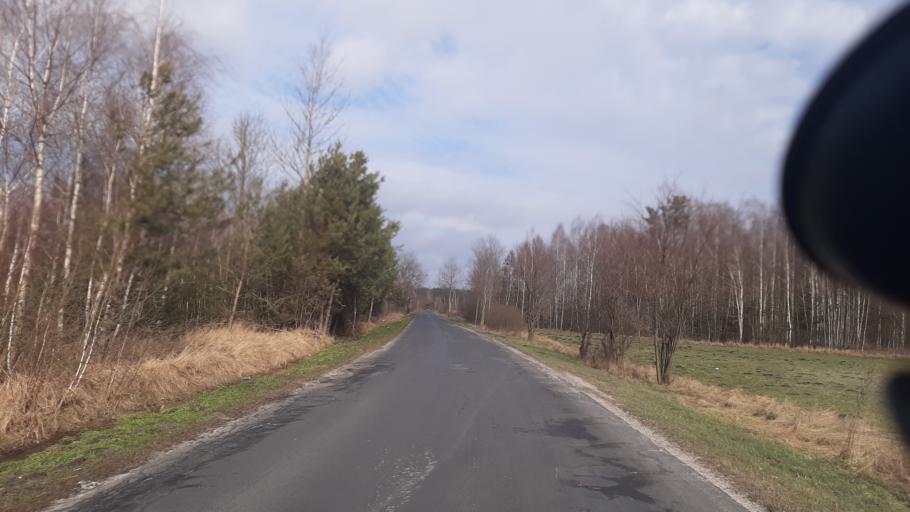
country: PL
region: Lublin Voivodeship
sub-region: Powiat lubartowski
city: Wola Sernicka
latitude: 51.4696
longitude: 22.7454
